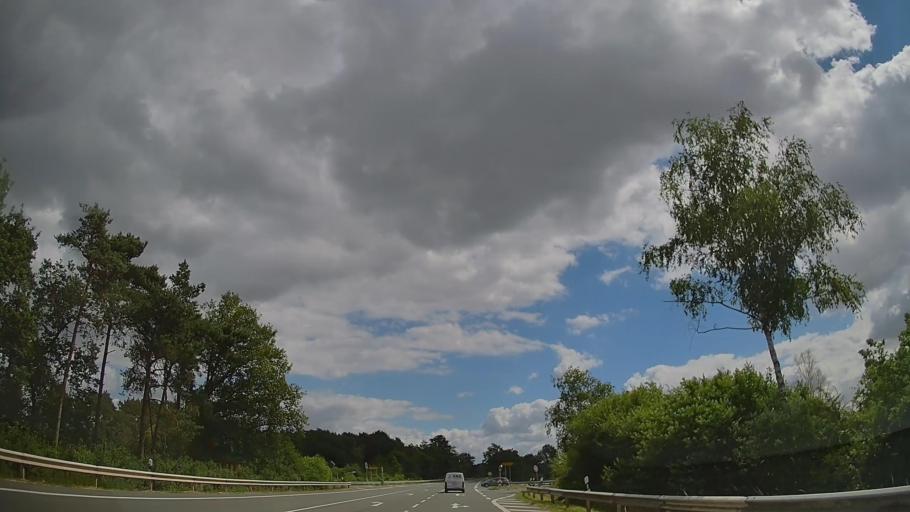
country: DE
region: North Rhine-Westphalia
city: Espelkamp
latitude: 52.3961
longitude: 8.5994
